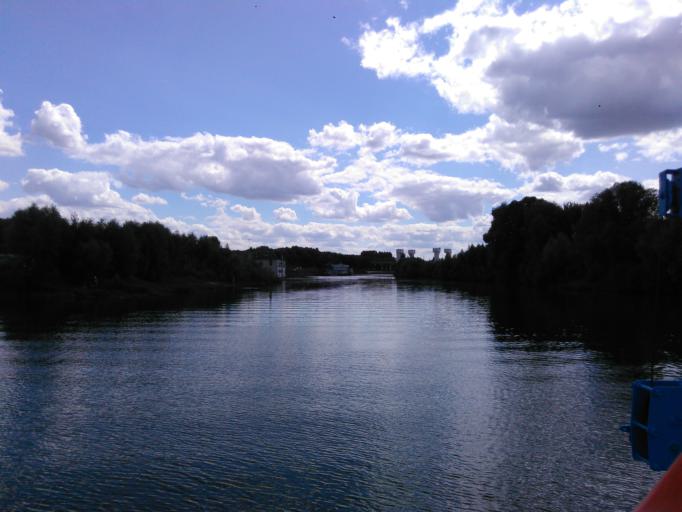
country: RU
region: Rjazan
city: Ryazan'
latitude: 54.6496
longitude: 39.7645
